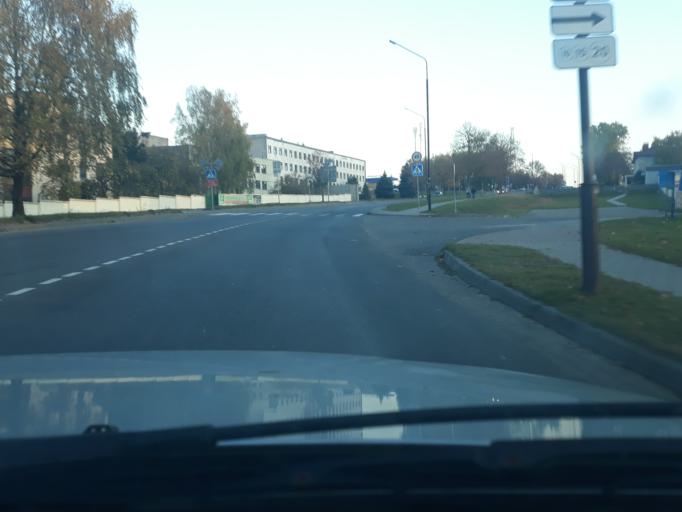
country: BY
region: Grodnenskaya
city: Vawkavysk
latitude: 53.1522
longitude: 24.4579
